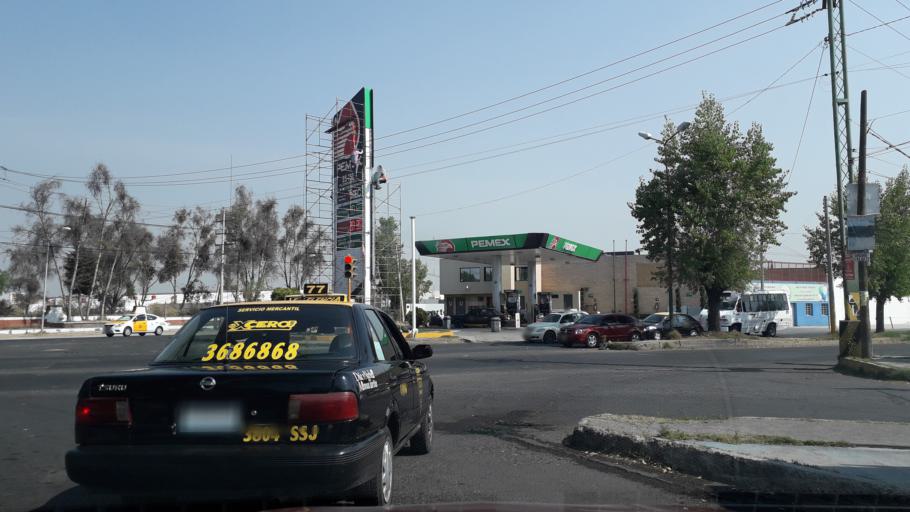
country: MX
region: Puebla
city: Puebla
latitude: 19.0794
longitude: -98.2163
